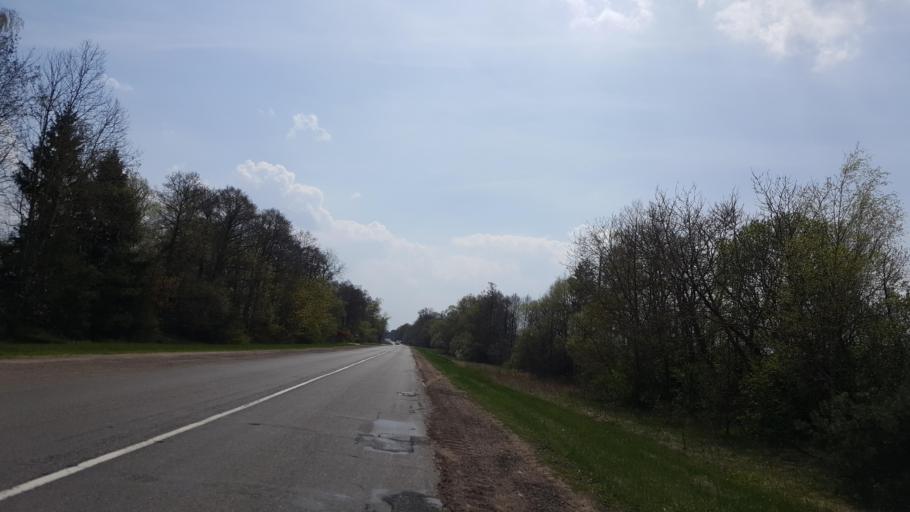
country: BY
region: Brest
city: Zhabinka
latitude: 52.2395
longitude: 23.9778
